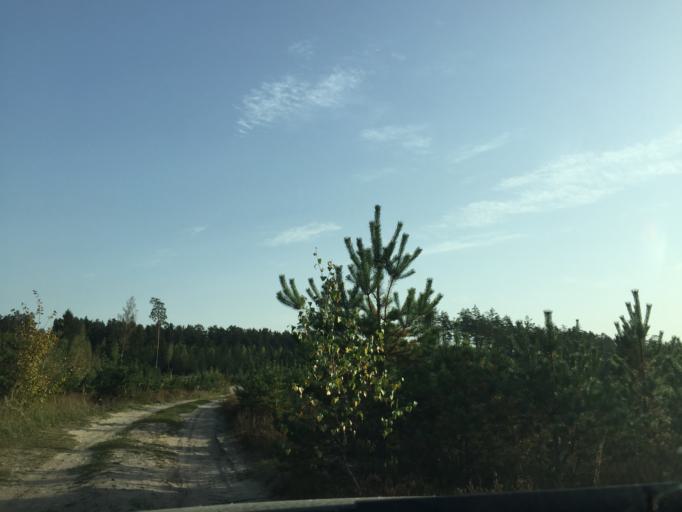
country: LV
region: Garkalne
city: Garkalne
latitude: 56.9685
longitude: 24.4207
